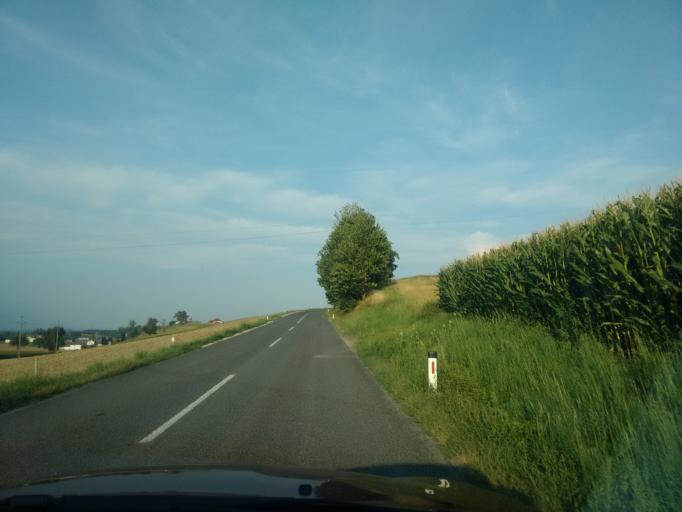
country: AT
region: Upper Austria
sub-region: Politischer Bezirk Vocklabruck
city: Niederthalheim
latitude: 48.1412
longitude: 13.7212
